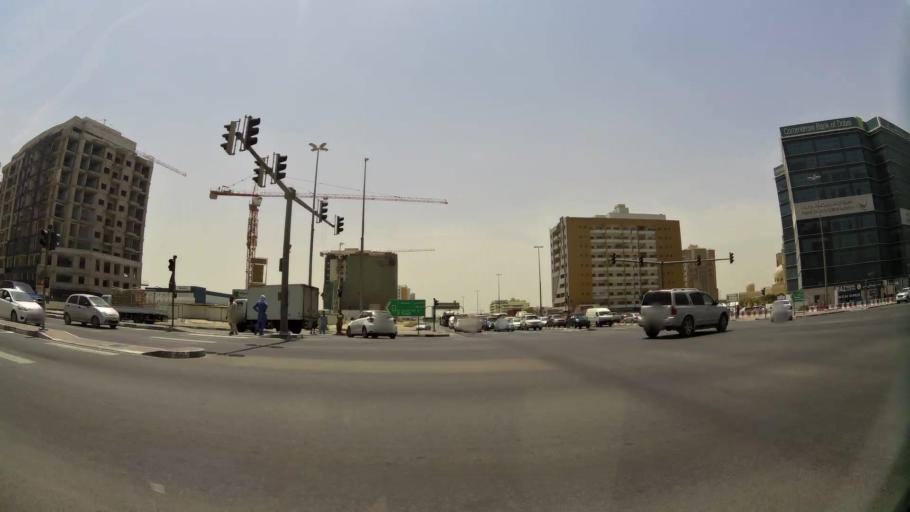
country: AE
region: Ash Shariqah
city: Sharjah
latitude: 25.2888
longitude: 55.4008
